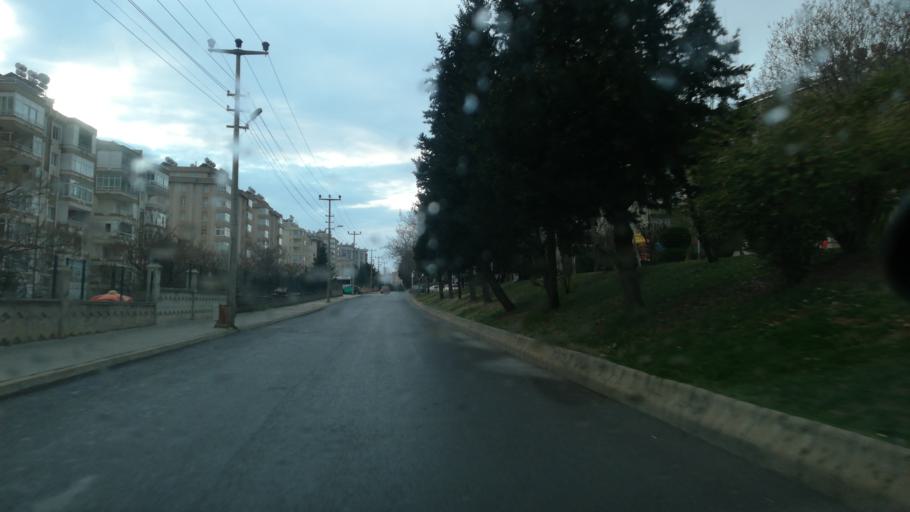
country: TR
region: Kahramanmaras
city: Kahramanmaras
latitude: 37.5880
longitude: 36.8952
